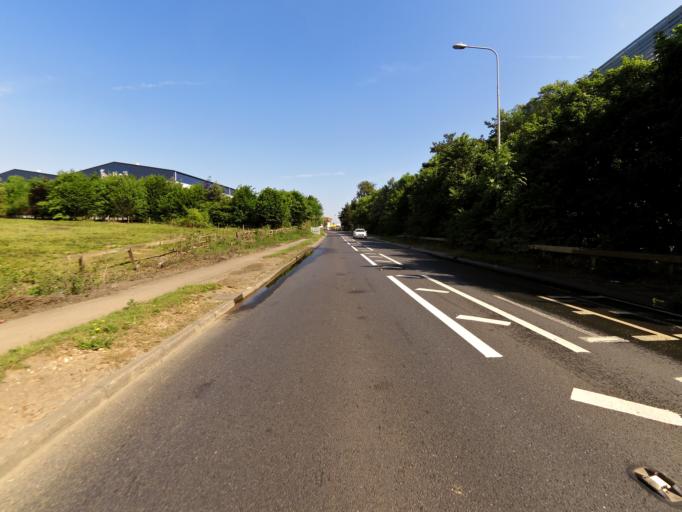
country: GB
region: England
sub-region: Suffolk
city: Bramford
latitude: 52.1036
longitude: 1.0976
